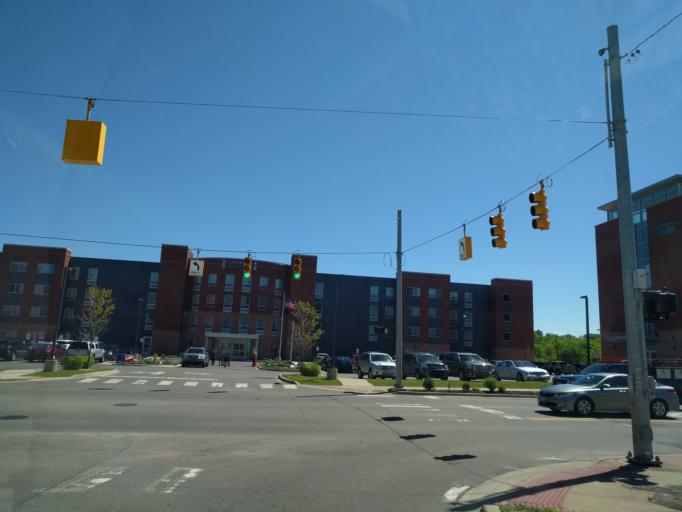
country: US
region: Michigan
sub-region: Marquette County
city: Marquette
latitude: 46.5460
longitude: -87.4123
